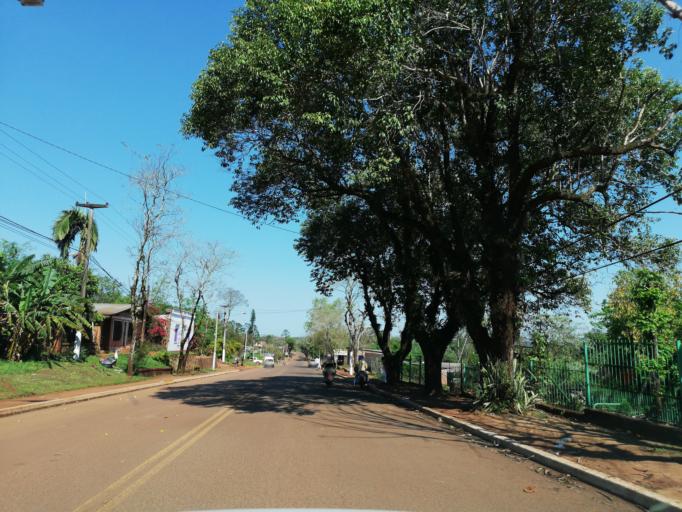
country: AR
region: Misiones
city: Puerto Eldorado
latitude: -26.4093
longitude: -54.6758
